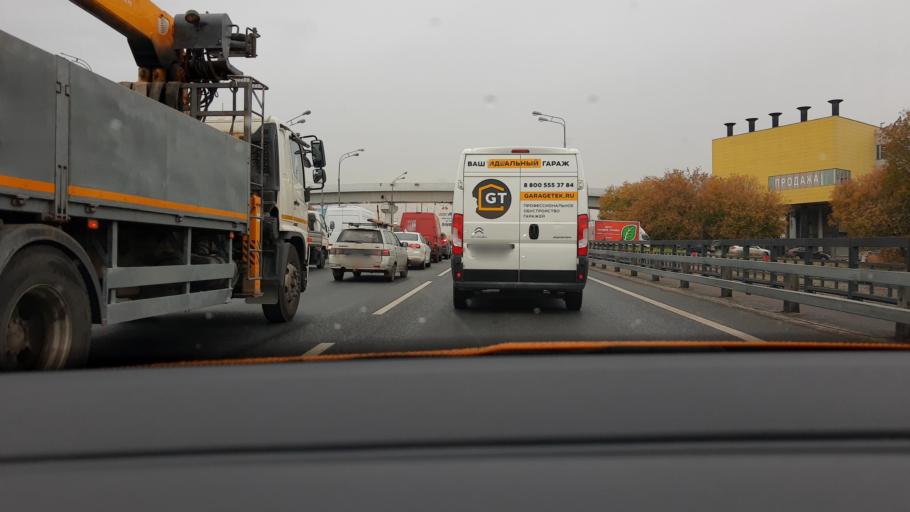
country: RU
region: Moscow
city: Strogino
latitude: 55.8297
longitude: 37.3956
